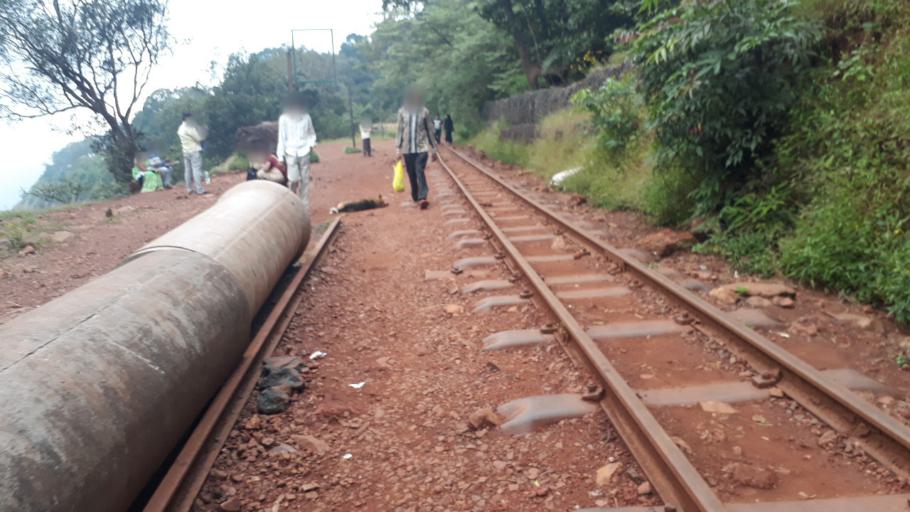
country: IN
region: Maharashtra
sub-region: Raigarh
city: Matheran
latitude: 19.0002
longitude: 73.2780
